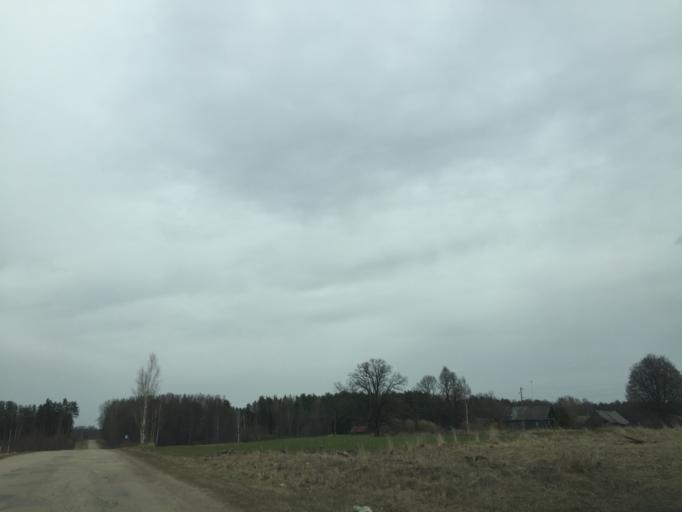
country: LV
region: Ilukste
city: Ilukste
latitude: 56.0359
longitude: 26.2768
